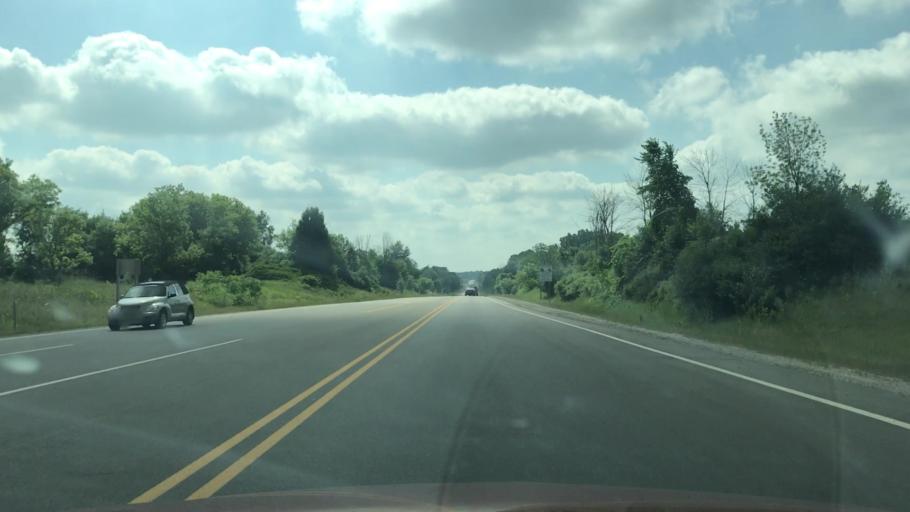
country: US
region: Michigan
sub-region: Kent County
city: Kent City
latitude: 43.2117
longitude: -85.7504
